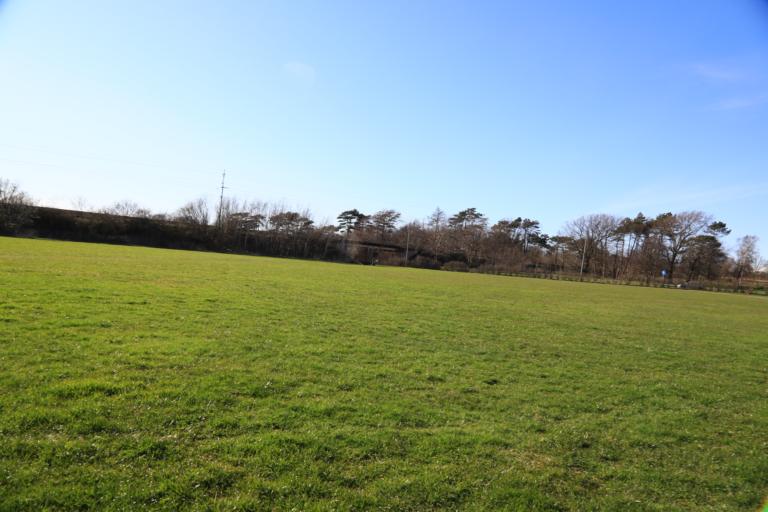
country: SE
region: Halland
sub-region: Varbergs Kommun
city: Varberg
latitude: 57.0987
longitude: 12.2468
